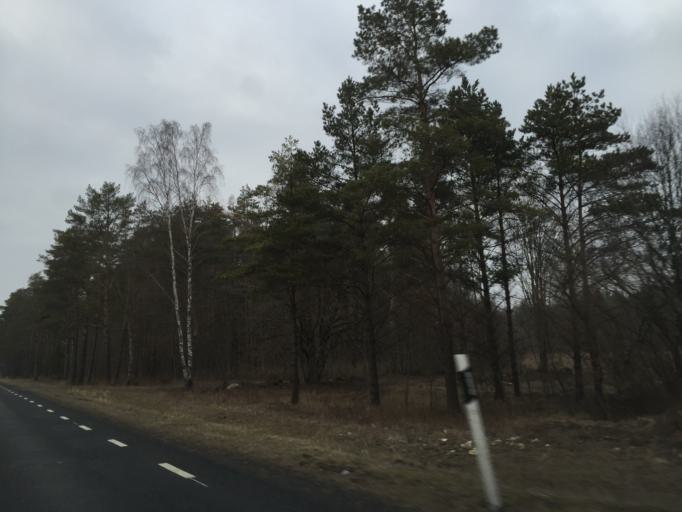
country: EE
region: Saare
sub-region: Orissaare vald
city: Orissaare
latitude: 58.5947
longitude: 23.3283
